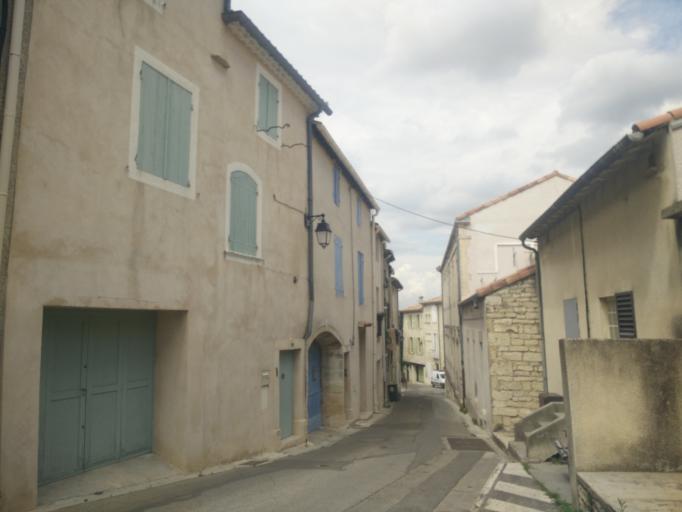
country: FR
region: Languedoc-Roussillon
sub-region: Departement du Gard
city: Calvisson
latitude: 43.7839
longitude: 4.1904
